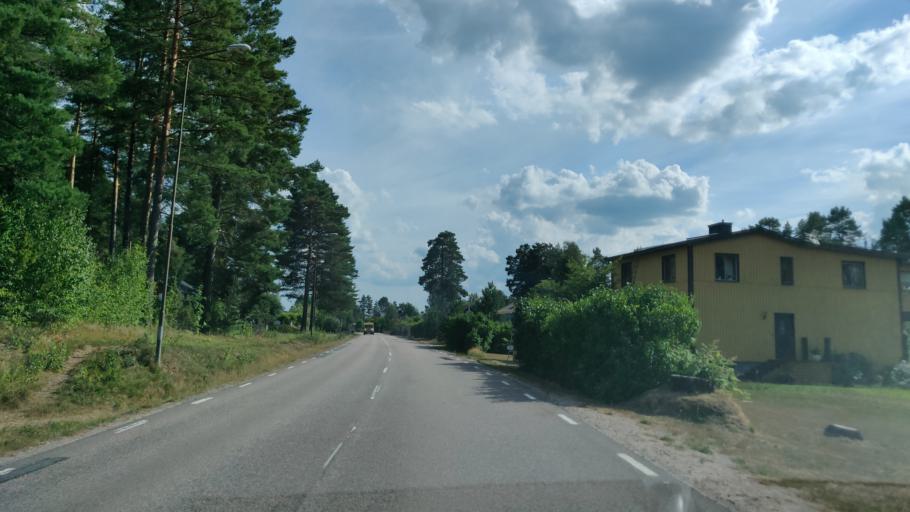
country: SE
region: Vaermland
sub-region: Hagfors Kommun
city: Ekshaerad
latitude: 60.1184
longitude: 13.5628
